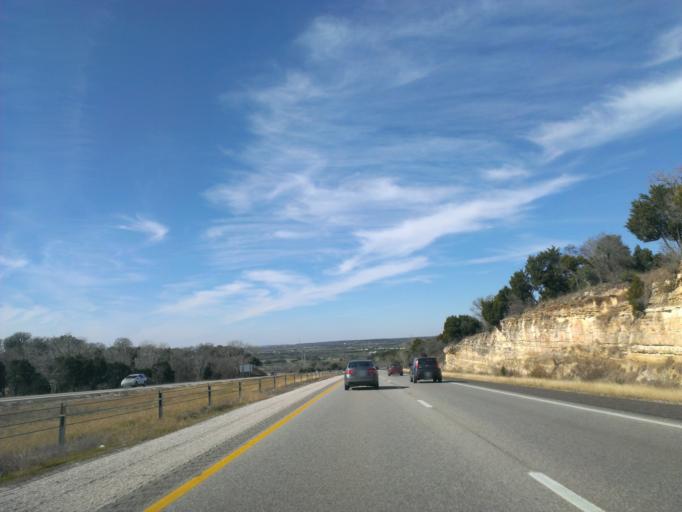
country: US
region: Texas
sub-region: Bell County
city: Nolanville
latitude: 31.0572
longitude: -97.5583
